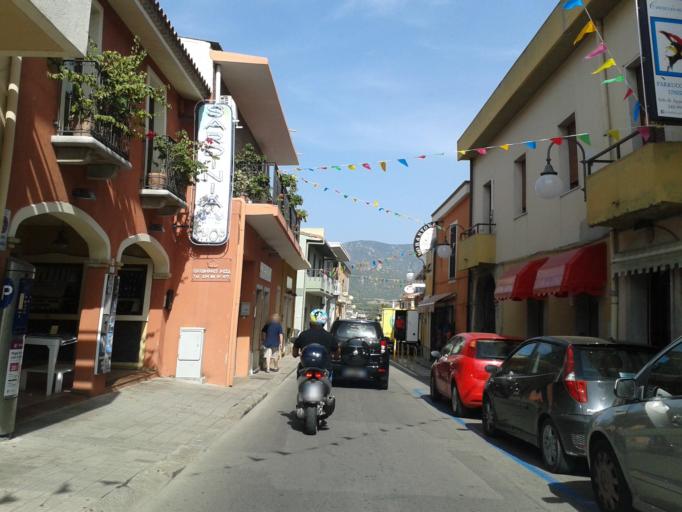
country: IT
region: Sardinia
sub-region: Provincia di Cagliari
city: Villasimius
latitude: 39.1441
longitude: 9.5185
